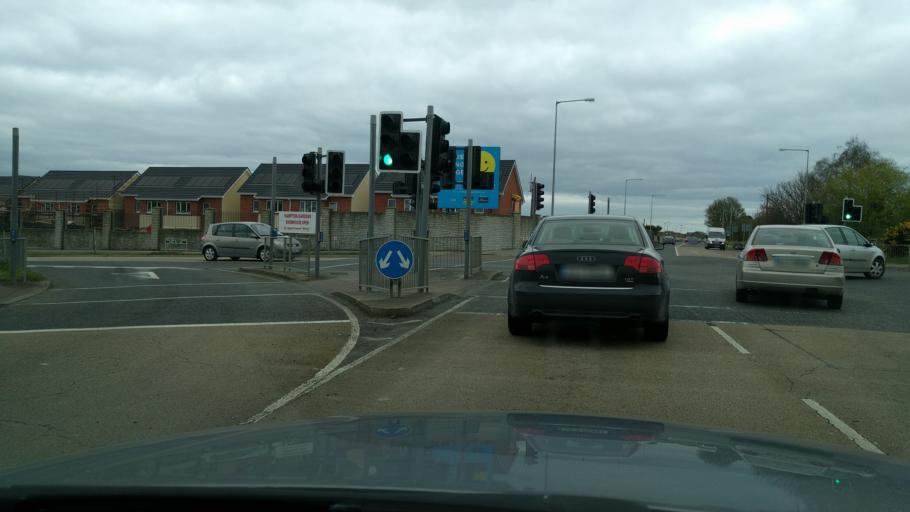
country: IE
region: Leinster
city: Balbriggan
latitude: 53.6070
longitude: -6.2028
